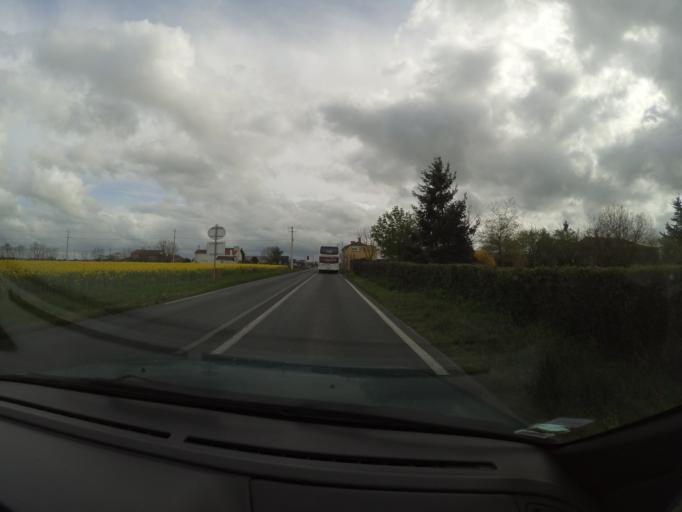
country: FR
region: Pays de la Loire
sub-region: Departement de Maine-et-Loire
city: Lire
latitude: 47.3271
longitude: -1.1668
